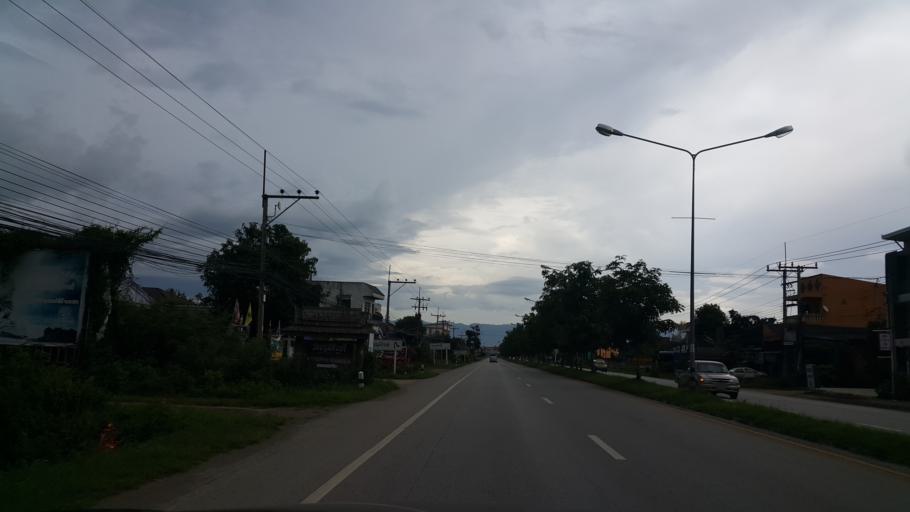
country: TH
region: Phayao
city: Dok Kham Tai
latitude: 19.1617
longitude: 99.9789
